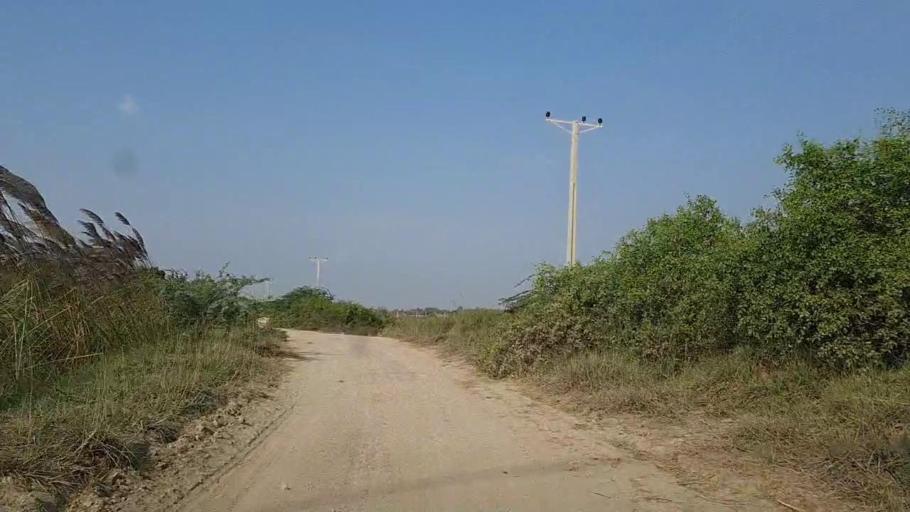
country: PK
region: Sindh
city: Mirpur Sakro
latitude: 24.5801
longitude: 67.5678
